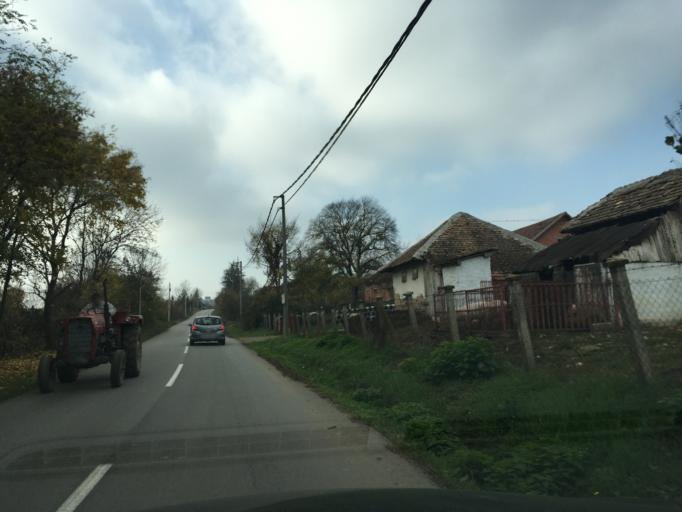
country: RS
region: Central Serbia
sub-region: Belgrade
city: Sopot
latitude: 44.4951
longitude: 20.6087
